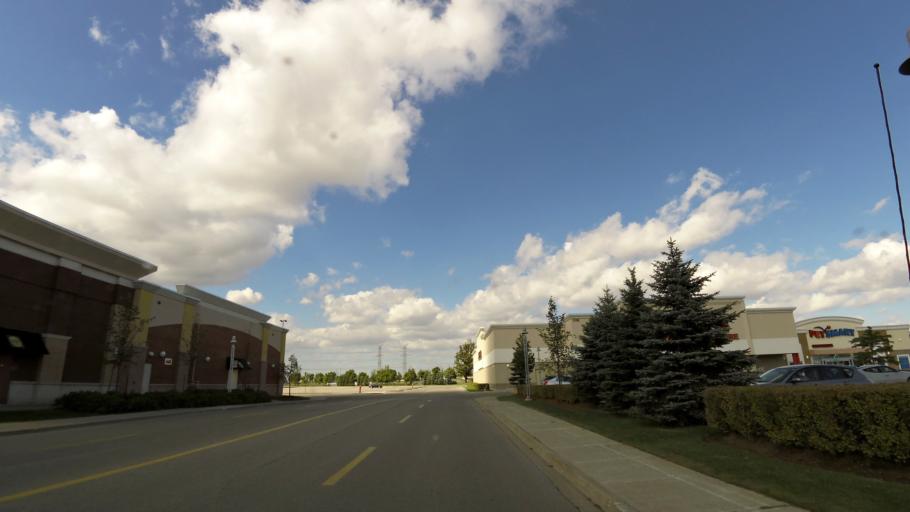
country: CA
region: Ontario
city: Brampton
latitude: 43.5971
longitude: -79.7882
